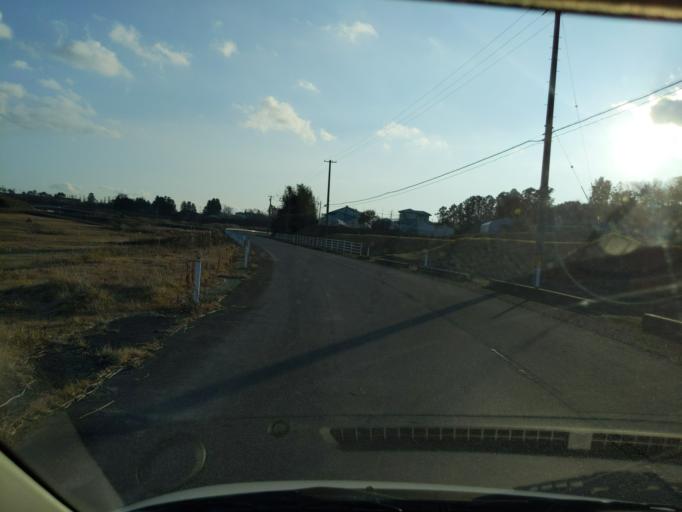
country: JP
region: Miyagi
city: Wakuya
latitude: 38.6790
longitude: 141.1094
